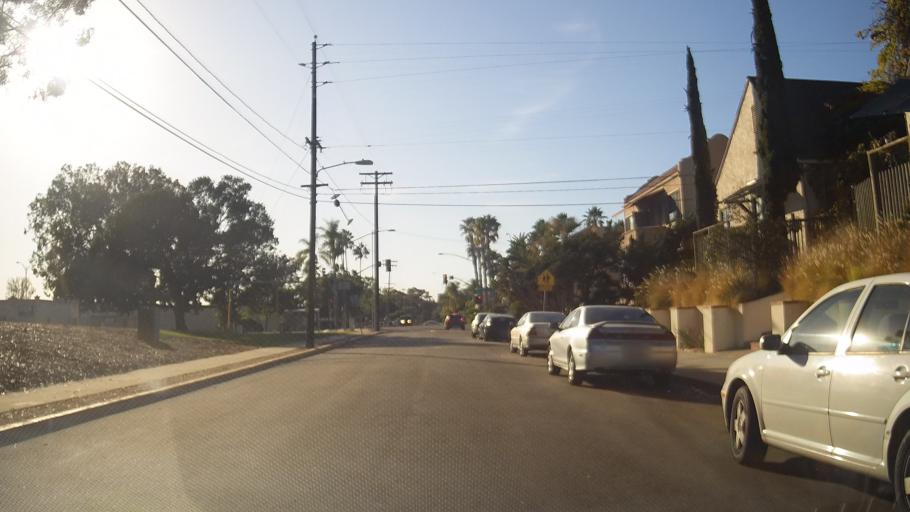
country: US
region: California
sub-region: San Diego County
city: San Diego
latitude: 32.7412
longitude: -117.1465
